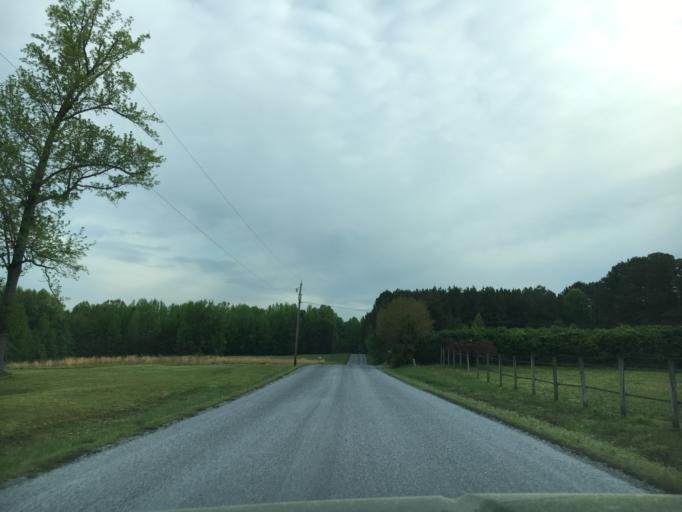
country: US
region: Virginia
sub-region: Campbell County
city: Brookneal
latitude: 36.9265
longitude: -78.9493
